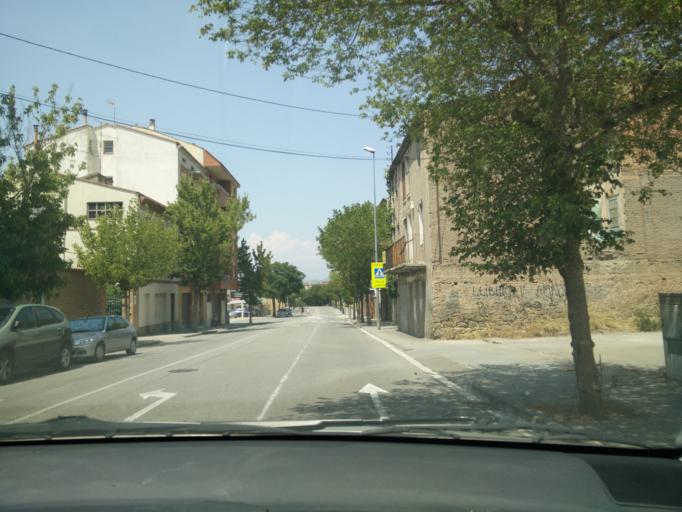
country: ES
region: Catalonia
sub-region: Provincia de Barcelona
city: Manresa
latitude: 41.7231
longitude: 1.8408
